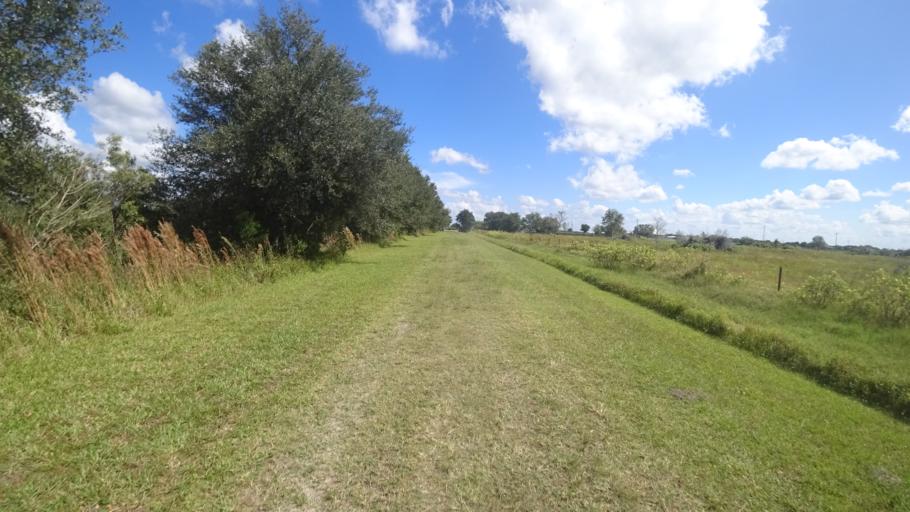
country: US
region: Florida
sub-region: Sarasota County
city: Warm Mineral Springs
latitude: 27.2858
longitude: -82.1947
